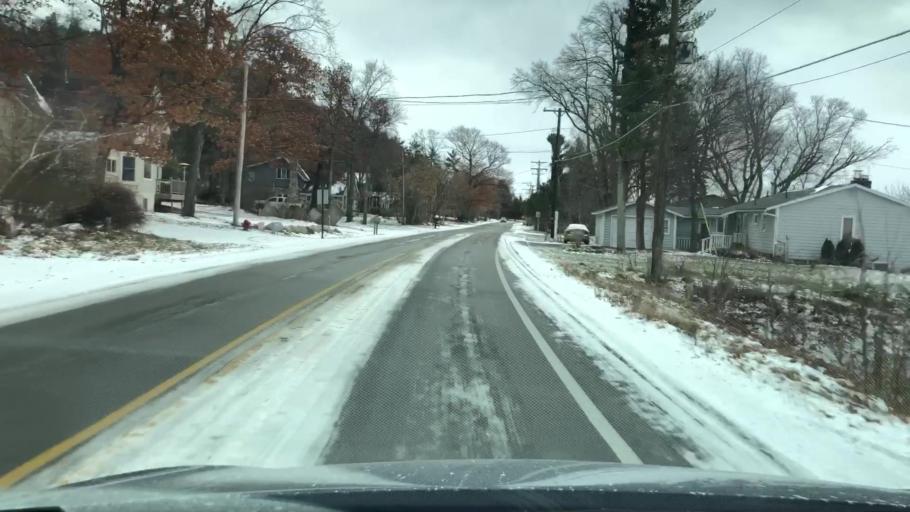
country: US
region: Michigan
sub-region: Grand Traverse County
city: Traverse City
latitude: 44.7895
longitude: -85.5875
